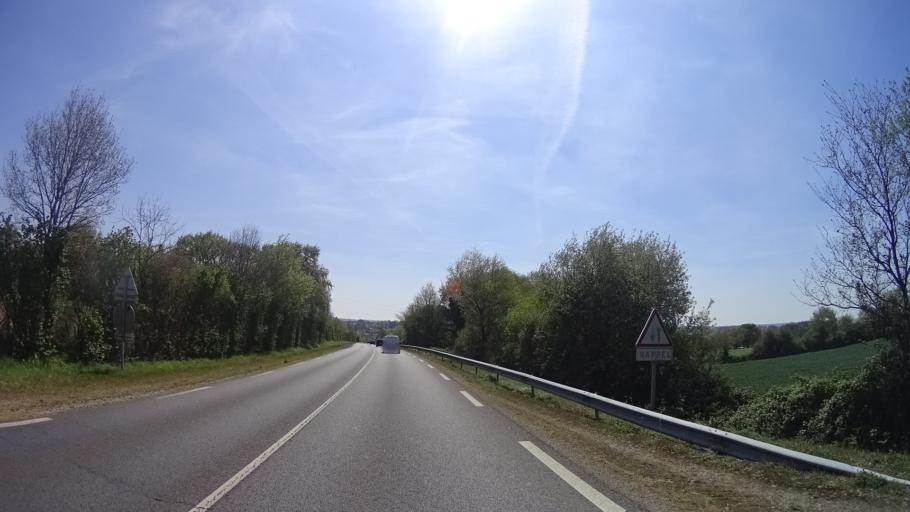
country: FR
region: Pays de la Loire
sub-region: Departement de la Loire-Atlantique
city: Fegreac
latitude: 47.5978
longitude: -2.0445
